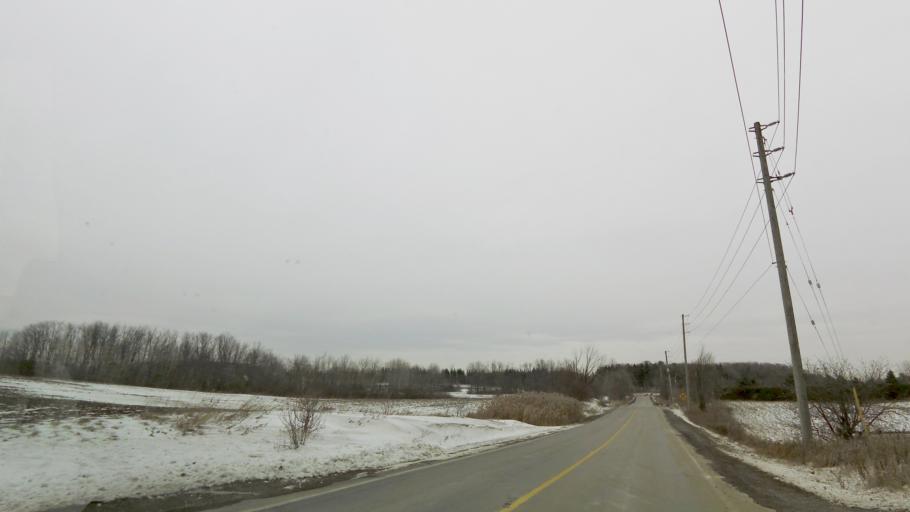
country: CA
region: Ontario
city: Vaughan
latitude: 43.8748
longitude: -79.5997
